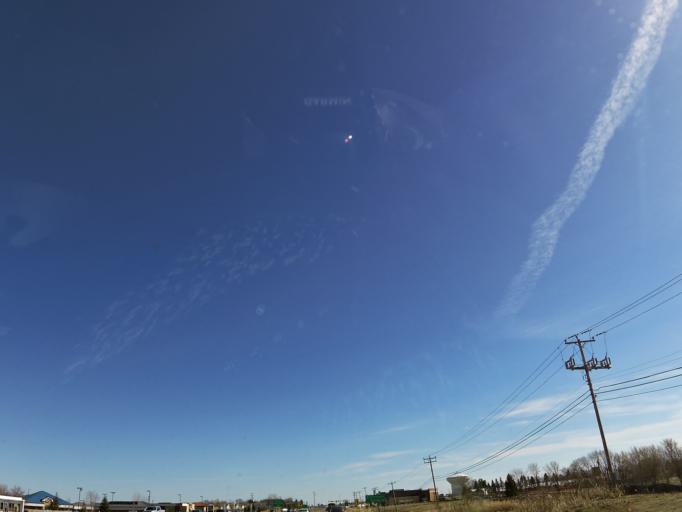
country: US
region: Minnesota
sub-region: Hennepin County
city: Wayzata
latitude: 45.0349
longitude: -93.5119
